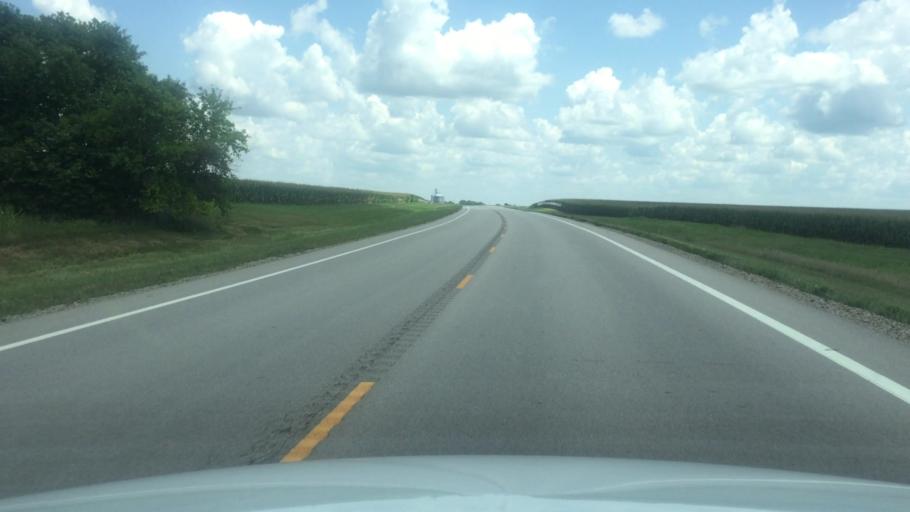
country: US
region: Kansas
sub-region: Brown County
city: Horton
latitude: 39.6603
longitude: -95.4057
